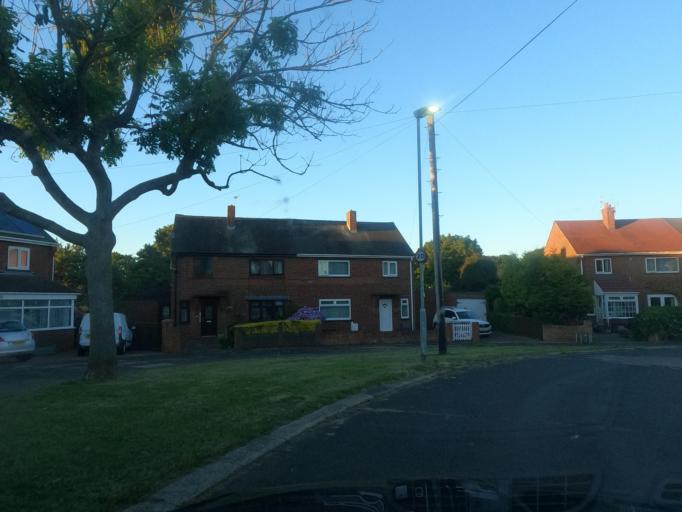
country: GB
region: England
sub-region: Northumberland
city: Newbiggin-by-the-Sea
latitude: 55.1803
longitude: -1.5233
